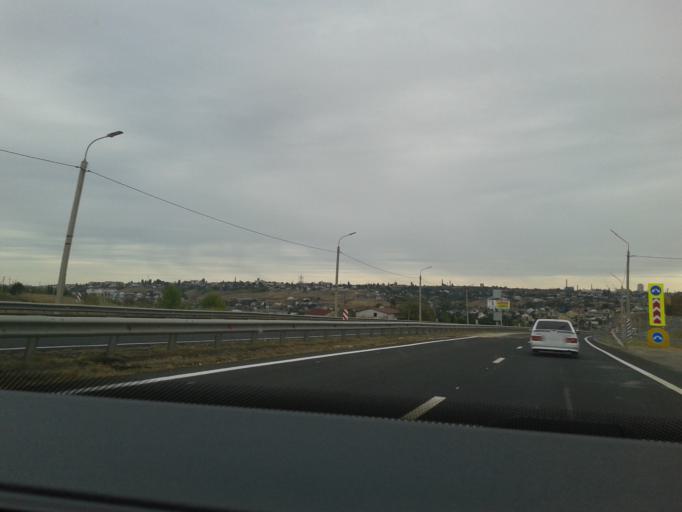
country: RU
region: Volgograd
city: Gorodishche
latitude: 48.8012
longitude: 44.4539
